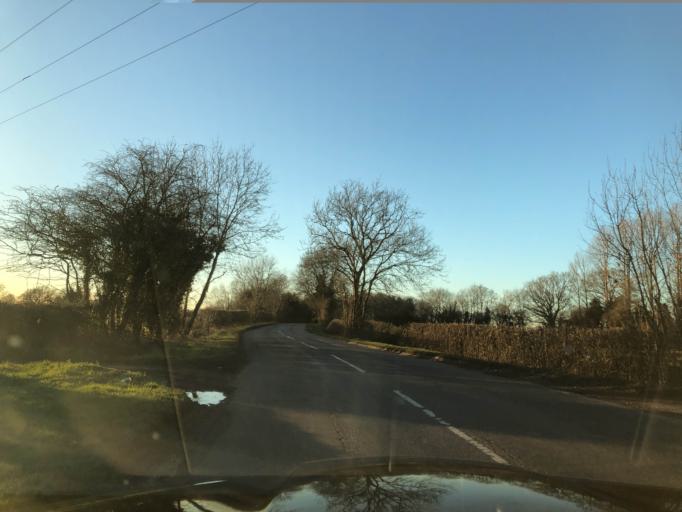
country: GB
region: England
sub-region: Warwickshire
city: Harbury
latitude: 52.2211
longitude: -1.4469
